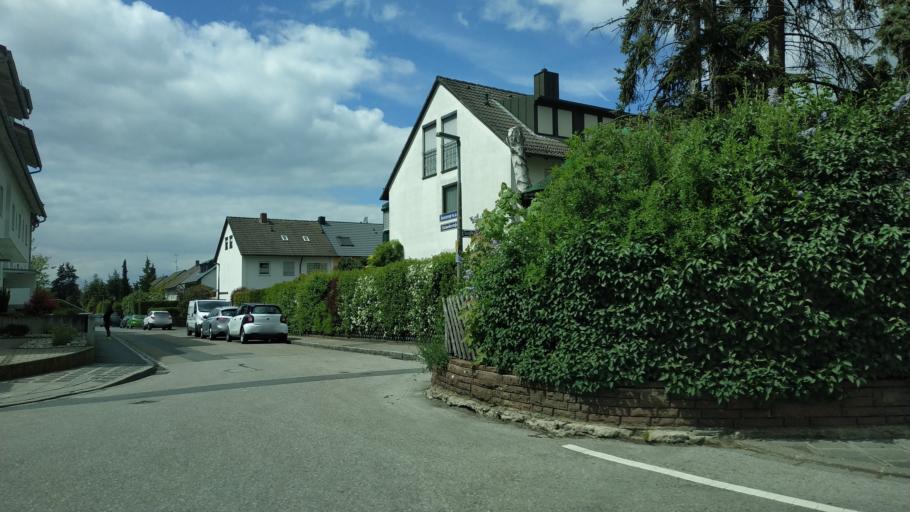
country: DE
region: Bavaria
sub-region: Regierungsbezirk Mittelfranken
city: Schwabach
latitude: 49.3723
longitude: 11.0787
